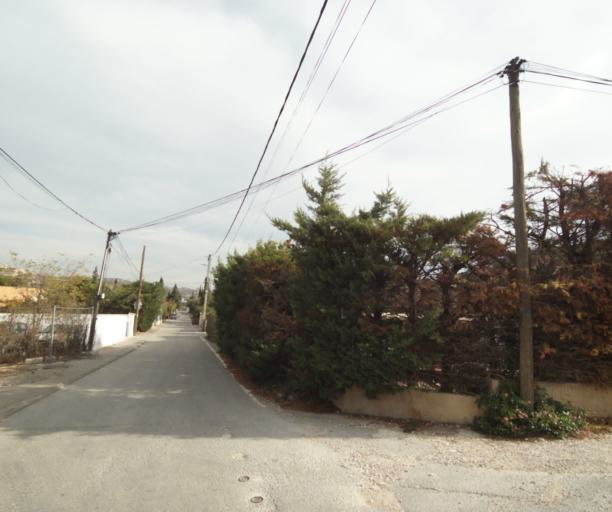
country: FR
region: Provence-Alpes-Cote d'Azur
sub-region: Departement des Bouches-du-Rhone
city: Le Rove
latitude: 43.3653
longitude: 5.2439
